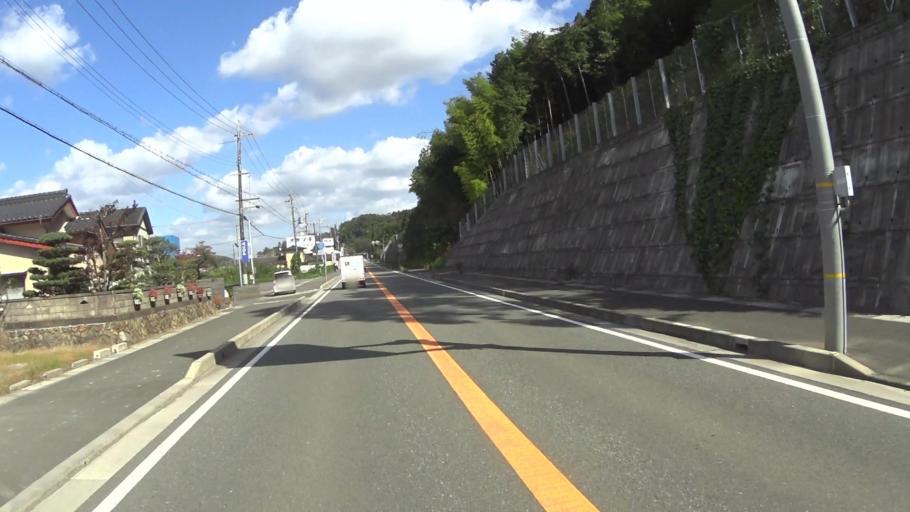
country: JP
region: Kyoto
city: Ayabe
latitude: 35.3017
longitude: 135.2700
